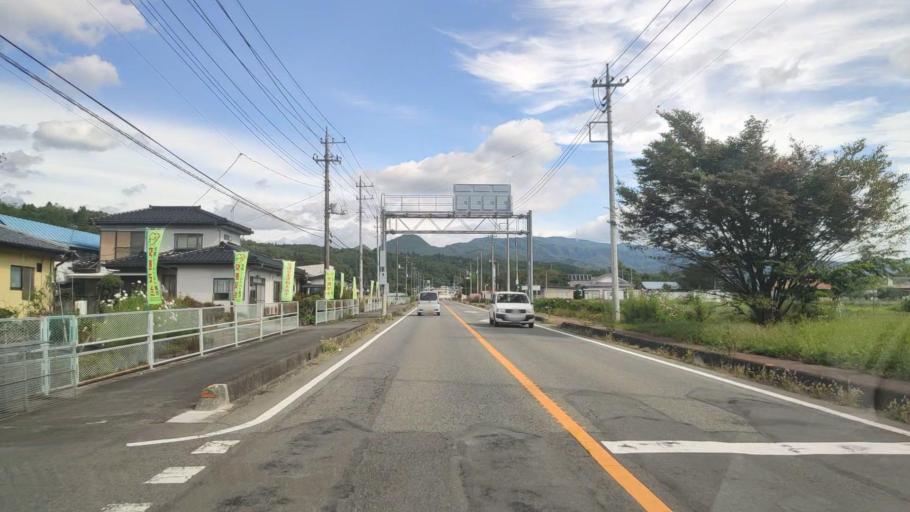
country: JP
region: Gunma
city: Nakanojomachi
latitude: 36.5959
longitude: 138.8626
